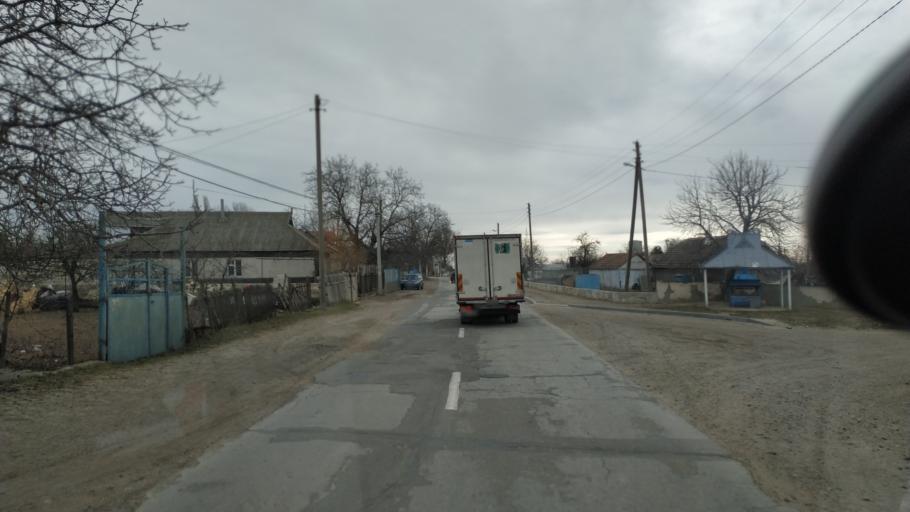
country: MD
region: Telenesti
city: Cocieri
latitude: 47.3150
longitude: 29.1048
